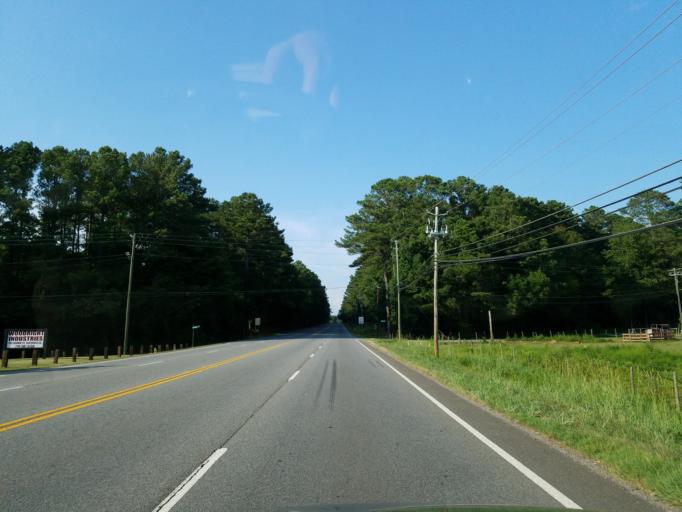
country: US
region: Georgia
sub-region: Bartow County
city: Cartersville
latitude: 34.2192
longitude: -84.7911
